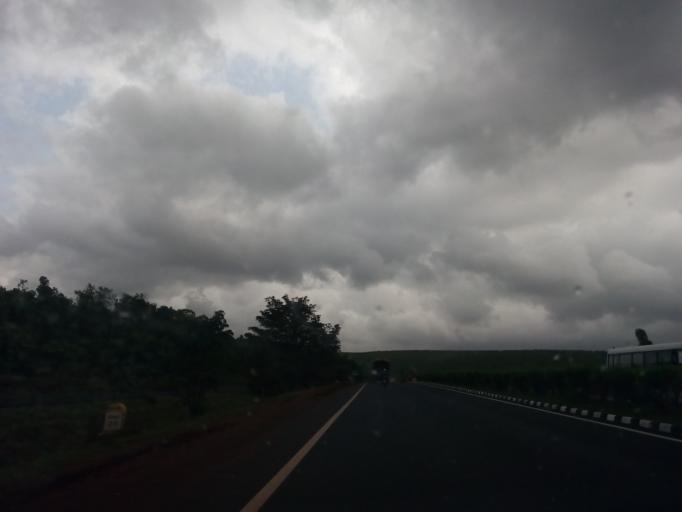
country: IN
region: Karnataka
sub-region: Belgaum
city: Hukeri
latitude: 16.0568
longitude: 74.5136
